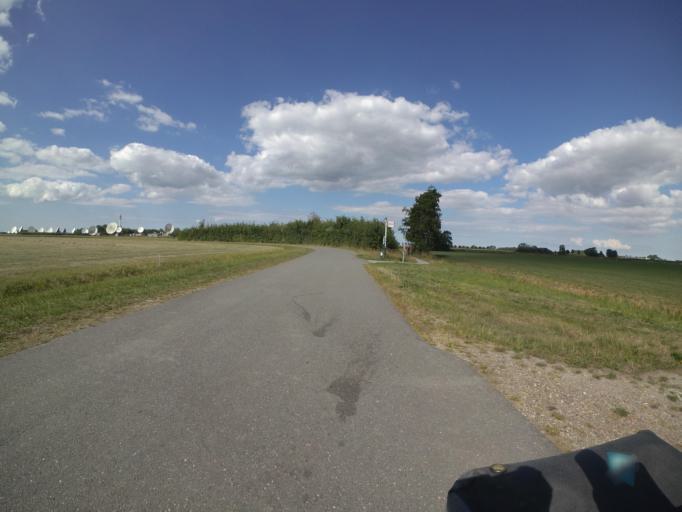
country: NL
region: Friesland
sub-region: Gemeente Kollumerland en Nieuwkruisland
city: Kollum
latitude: 53.2813
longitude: 6.2214
